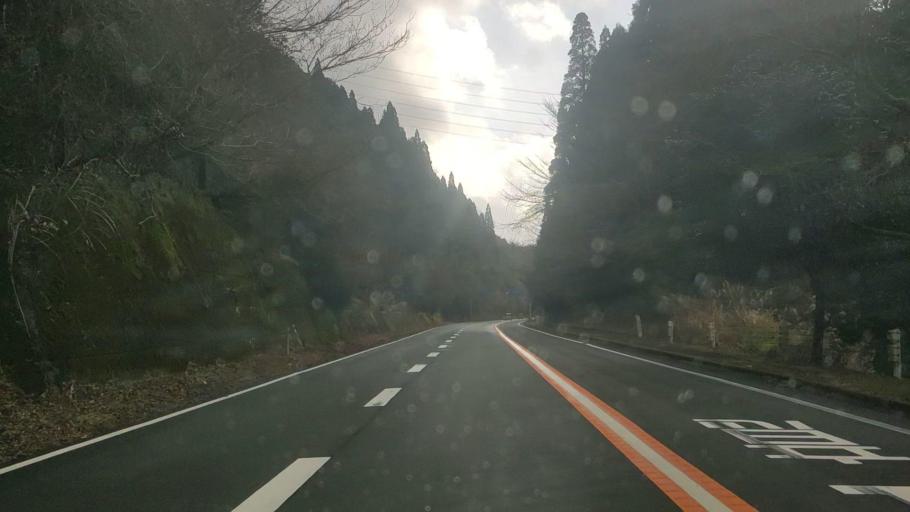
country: JP
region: Kumamoto
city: Hitoyoshi
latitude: 32.1118
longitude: 130.8054
